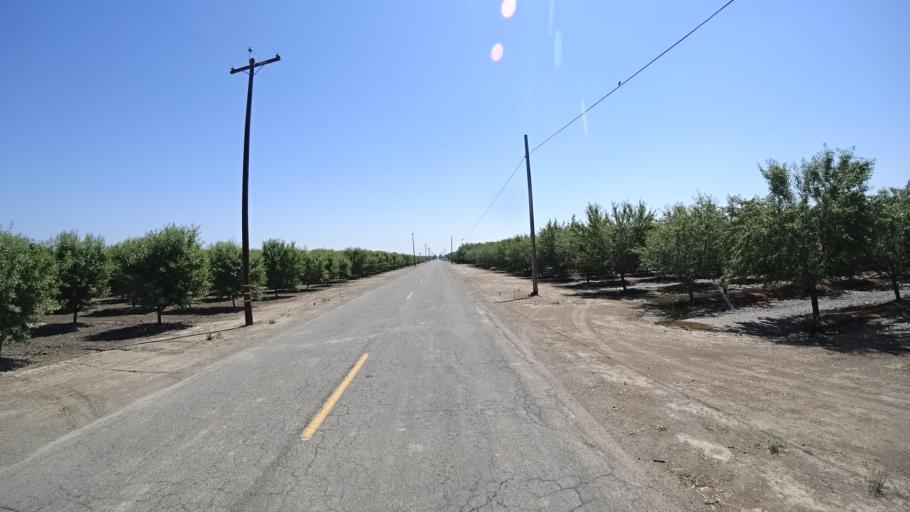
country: US
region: California
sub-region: Kings County
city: Armona
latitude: 36.3572
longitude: -119.7396
